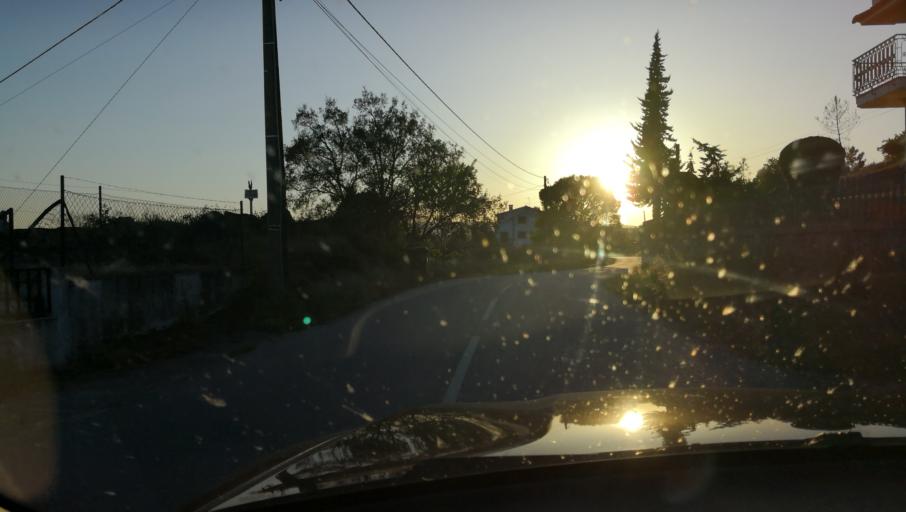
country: PT
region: Vila Real
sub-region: Mondim de Basto
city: Mondim de Basto
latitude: 41.4068
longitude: -7.9227
